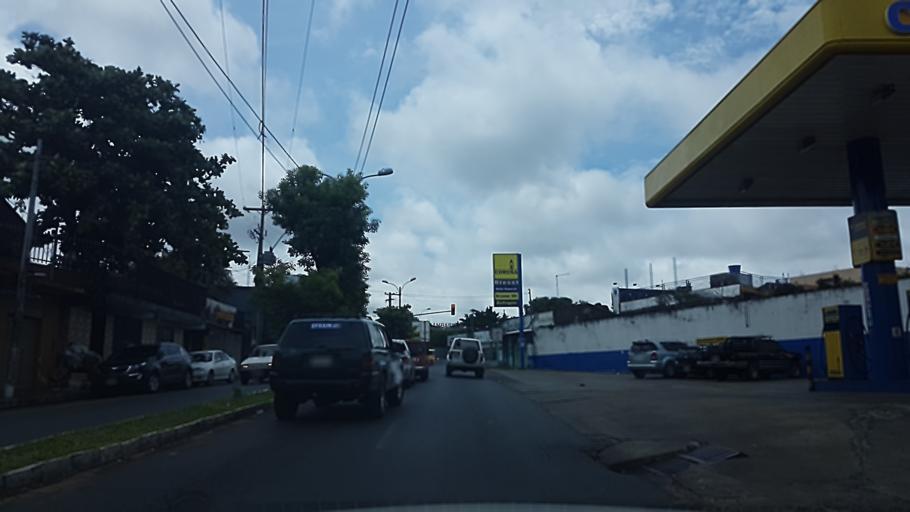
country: PY
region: Central
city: Villa Elisa
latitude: -25.3585
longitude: -57.5952
